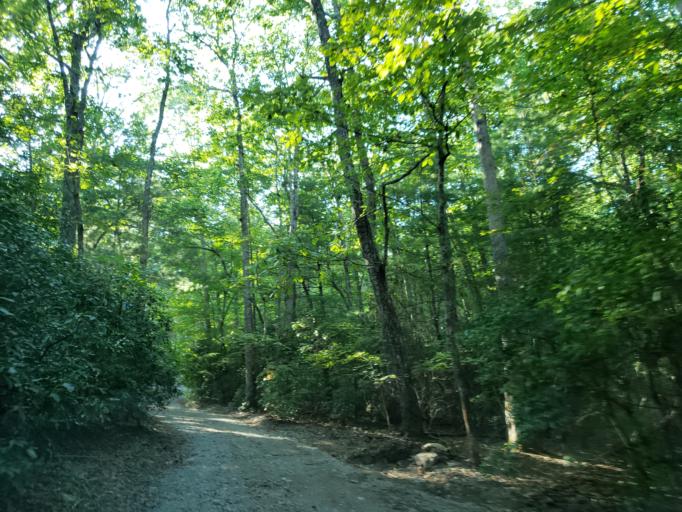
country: US
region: Georgia
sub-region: Fannin County
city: Blue Ridge
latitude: 34.6770
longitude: -84.2686
